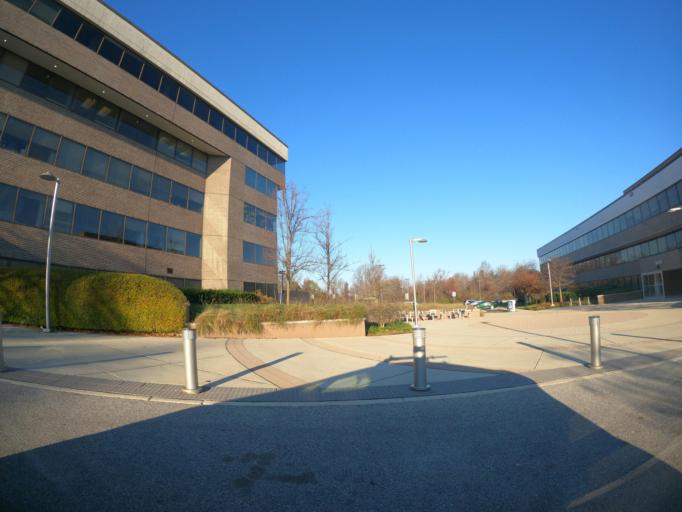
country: US
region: Maryland
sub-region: Howard County
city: Columbia
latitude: 39.2248
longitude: -76.8406
